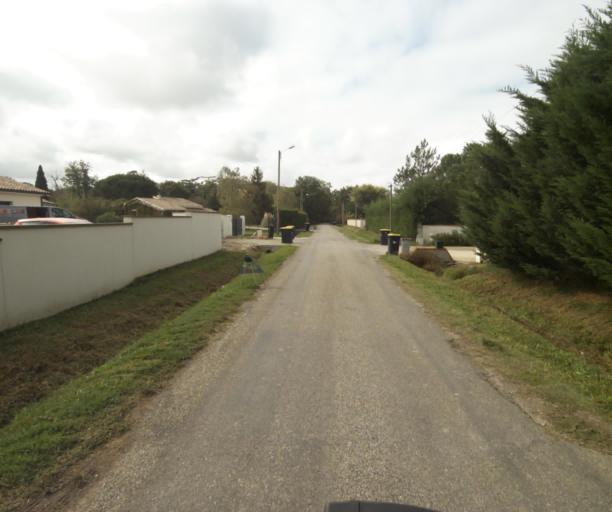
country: FR
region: Midi-Pyrenees
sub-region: Departement du Tarn-et-Garonne
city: Montech
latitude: 43.9575
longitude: 1.2524
